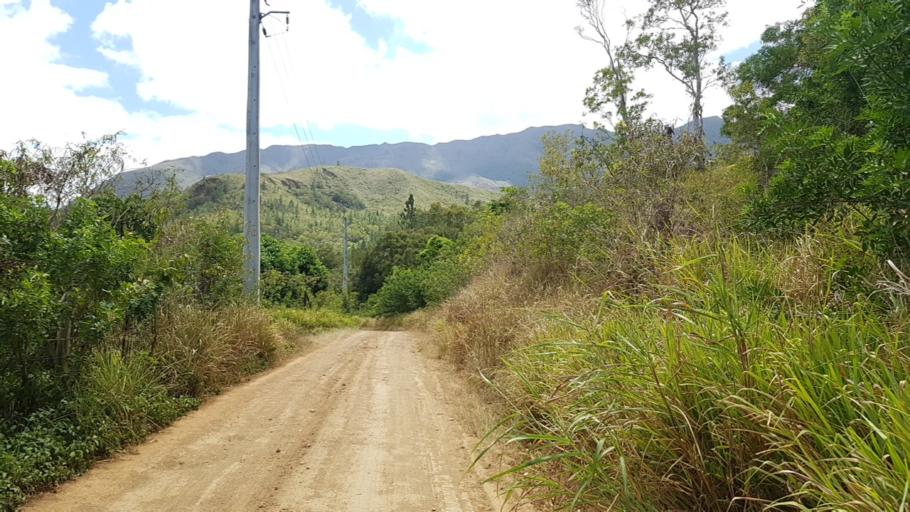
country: NC
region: South Province
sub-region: Dumbea
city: Dumbea
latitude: -22.1817
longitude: 166.4800
